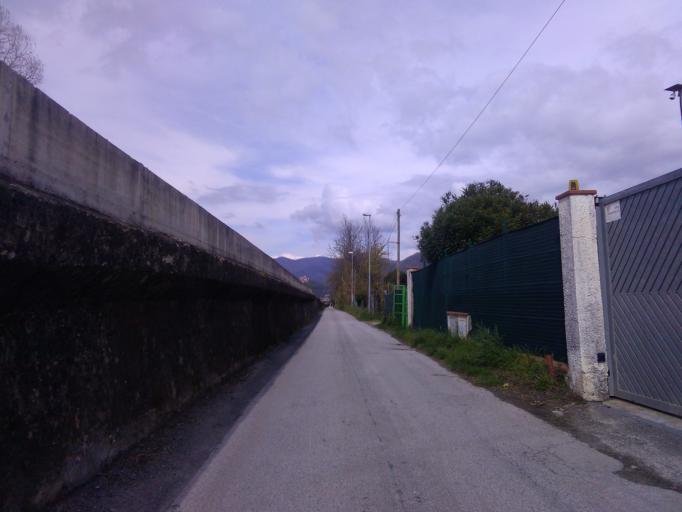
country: IT
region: Tuscany
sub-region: Provincia di Massa-Carrara
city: Marina di Carrara
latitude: 44.0495
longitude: 10.0221
